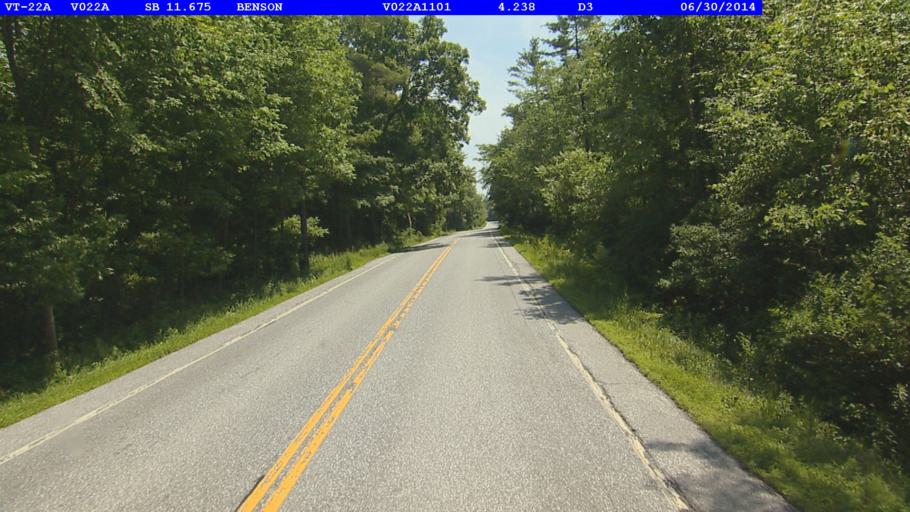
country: US
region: Vermont
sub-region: Rutland County
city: Fair Haven
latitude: 43.7290
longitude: -73.3026
